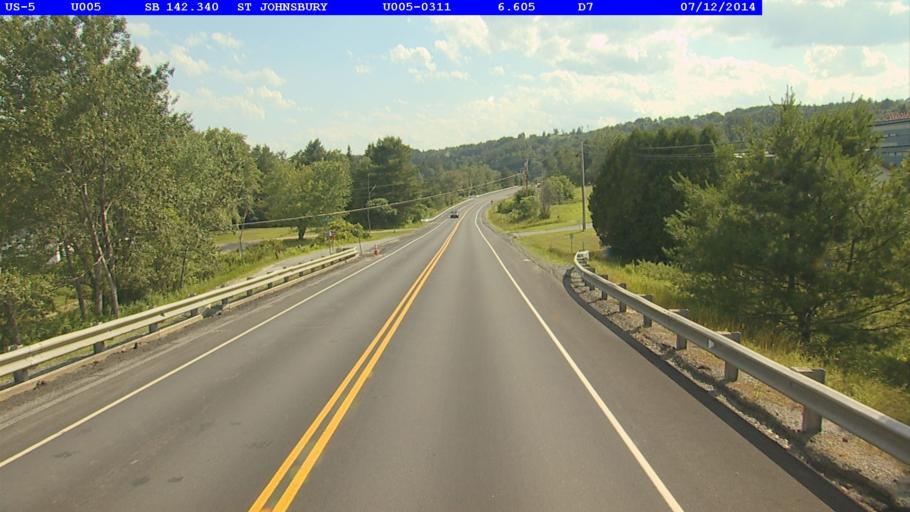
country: US
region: Vermont
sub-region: Caledonia County
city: Lyndon
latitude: 44.4847
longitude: -72.0117
